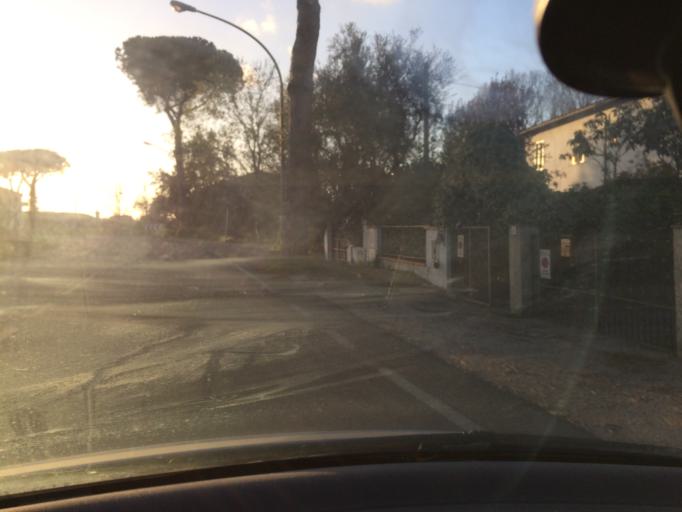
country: IT
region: Tuscany
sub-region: Province of Pisa
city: Gello
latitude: 43.7233
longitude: 10.4360
